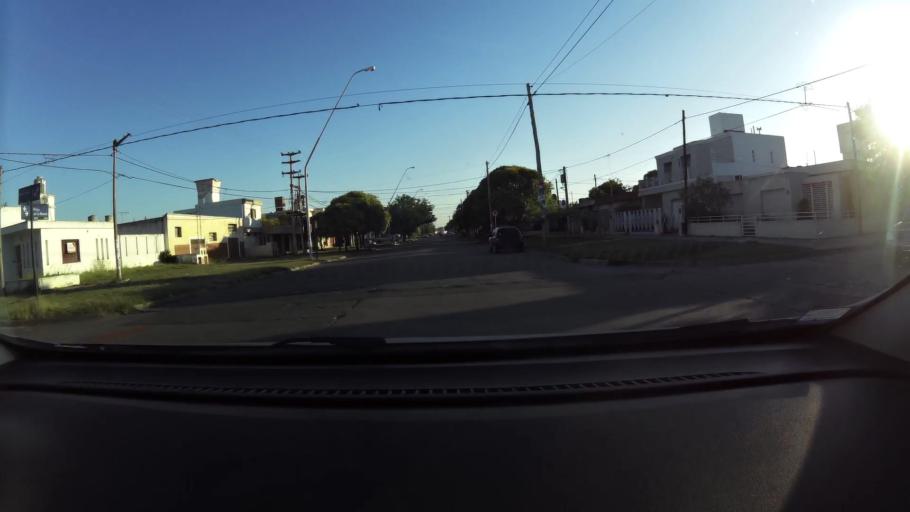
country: AR
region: Cordoba
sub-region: Departamento de Capital
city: Cordoba
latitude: -31.3753
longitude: -64.2140
